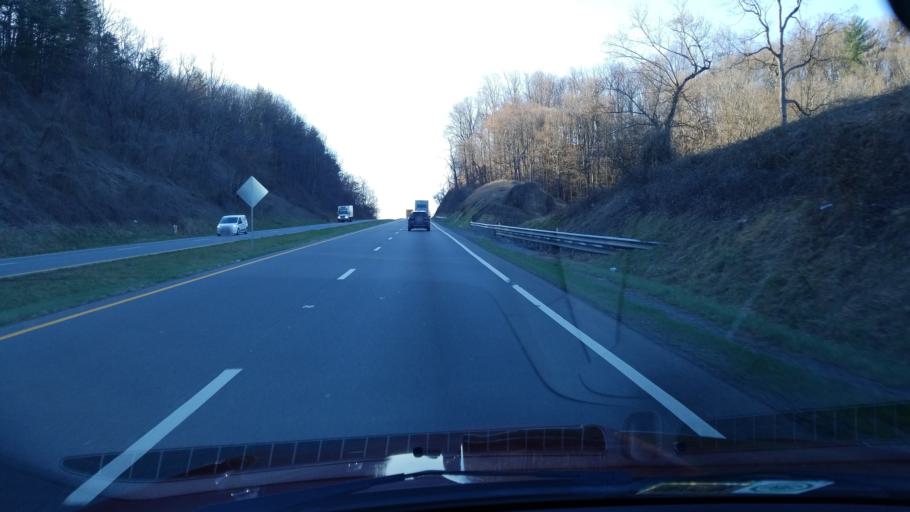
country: US
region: Virginia
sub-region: Roanoke County
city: Narrows
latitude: 37.1005
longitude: -79.9413
